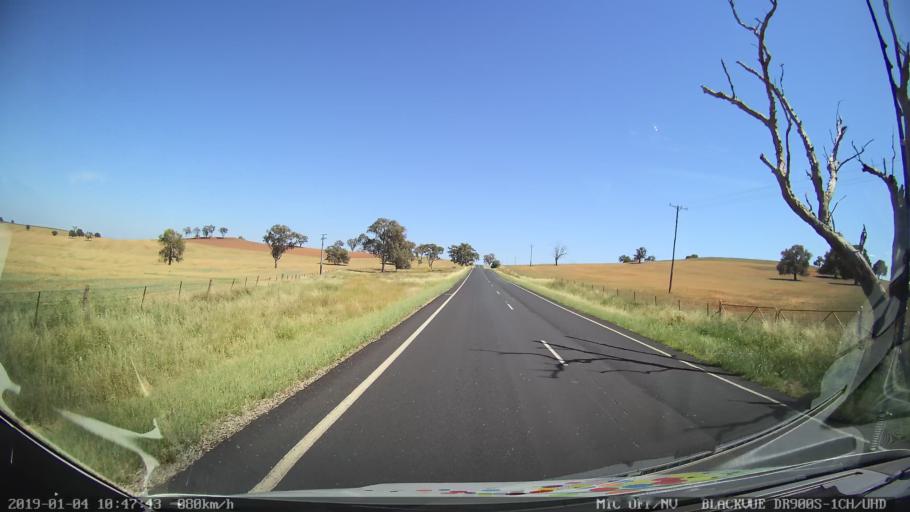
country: AU
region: New South Wales
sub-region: Cabonne
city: Molong
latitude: -33.2673
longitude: 148.7180
